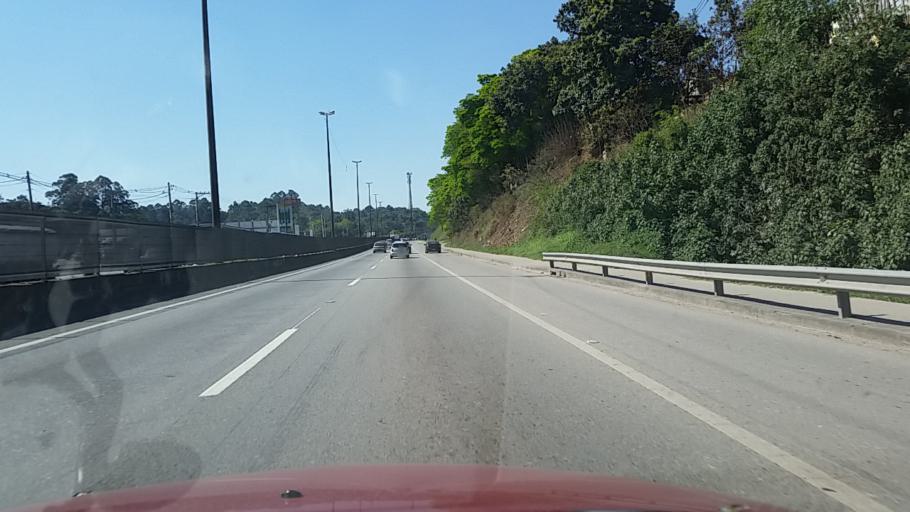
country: BR
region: Sao Paulo
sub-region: Taboao Da Serra
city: Taboao da Serra
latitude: -23.6245
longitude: -46.8157
